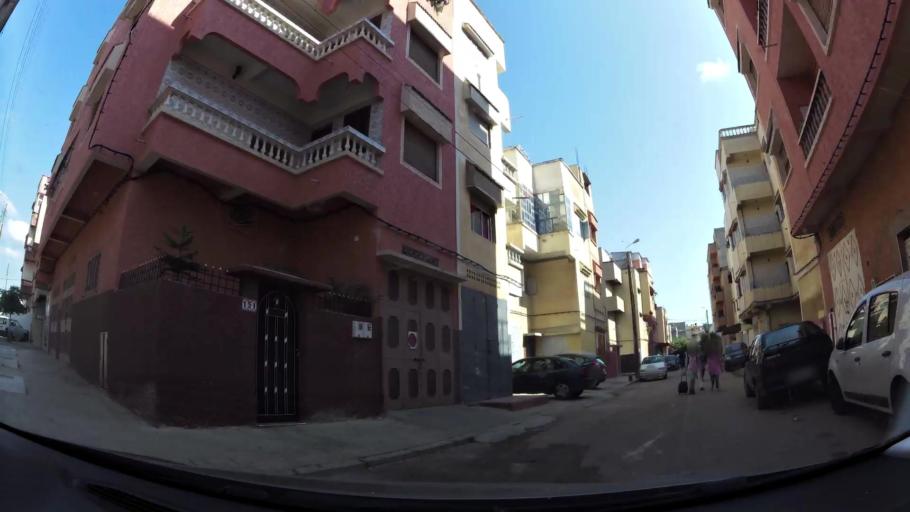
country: MA
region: Rabat-Sale-Zemmour-Zaer
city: Sale
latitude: 34.0450
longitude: -6.7780
